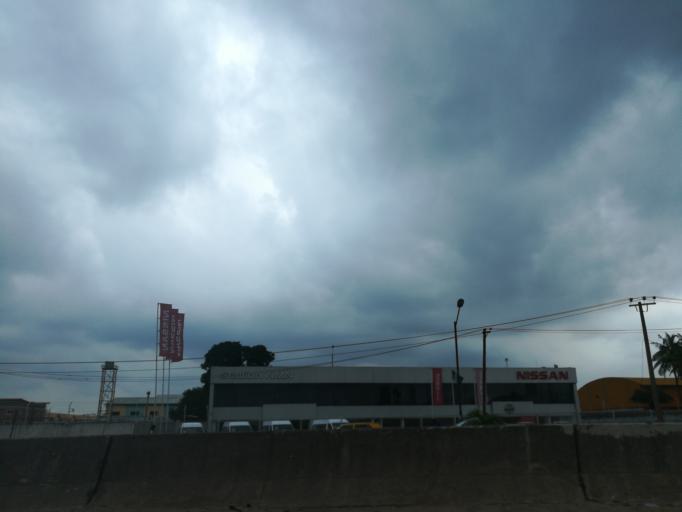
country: NG
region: Lagos
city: Somolu
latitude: 6.5523
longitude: 3.3750
